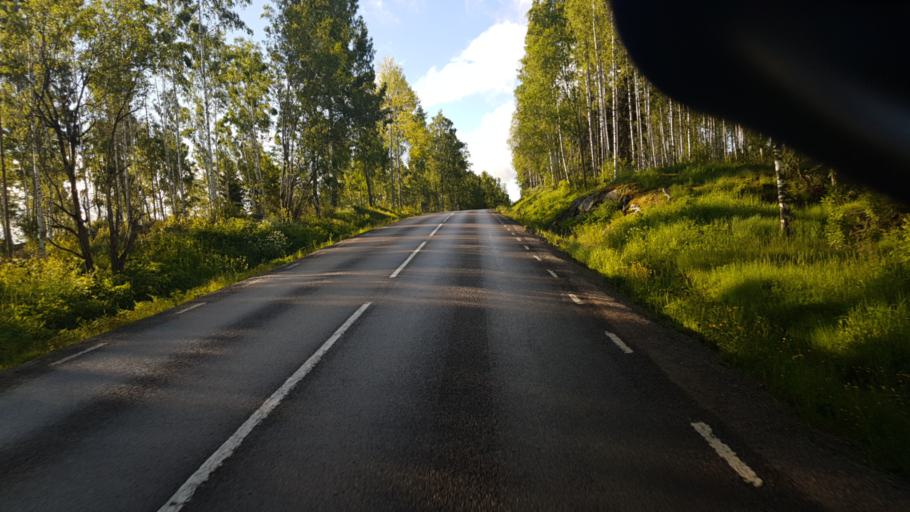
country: SE
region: Vaermland
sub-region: Arvika Kommun
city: Arvika
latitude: 59.6378
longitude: 12.4840
